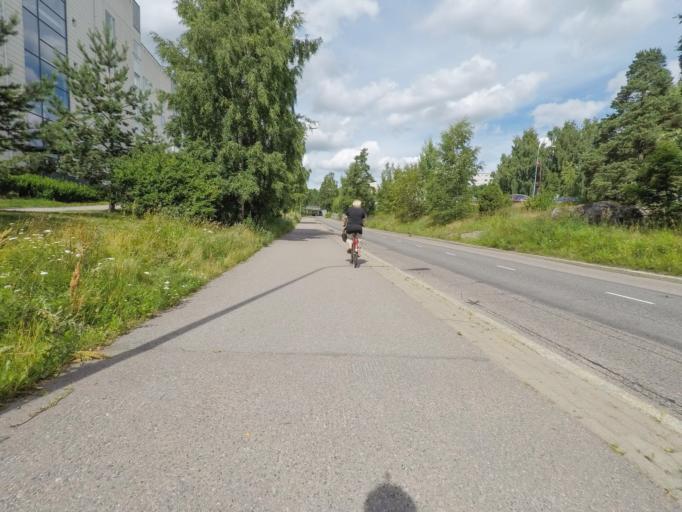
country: FI
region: Uusimaa
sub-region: Helsinki
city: Vantaa
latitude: 60.2284
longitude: 25.0011
